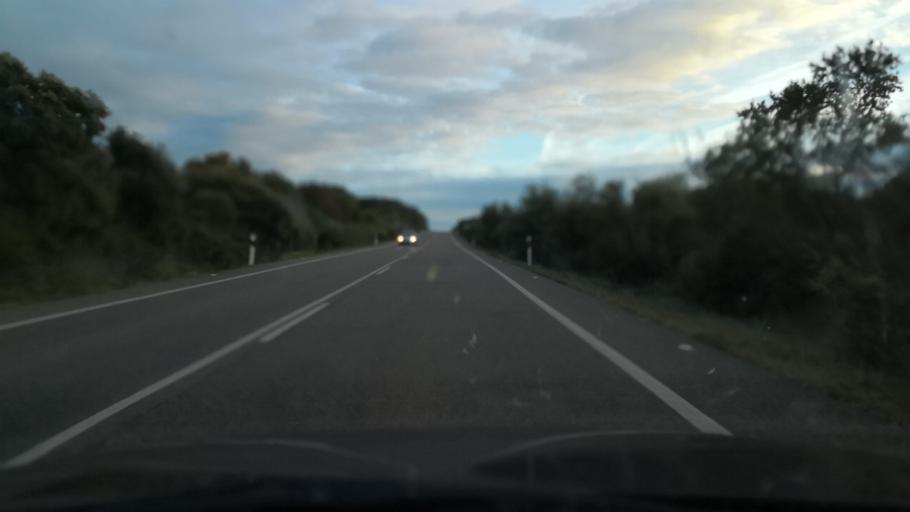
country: ES
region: Extremadura
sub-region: Provincia de Badajoz
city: La Roca de la Sierra
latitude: 39.1347
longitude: -6.6619
